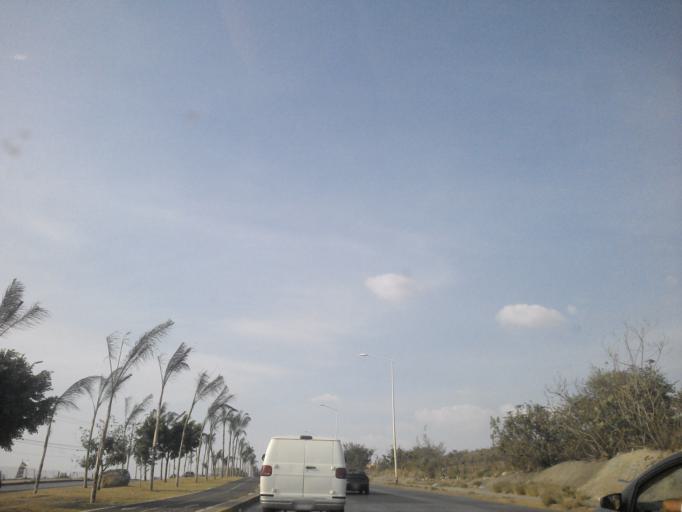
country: MX
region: Jalisco
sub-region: Tlajomulco de Zuniga
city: Altus Bosques
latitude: 20.5936
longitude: -103.3808
